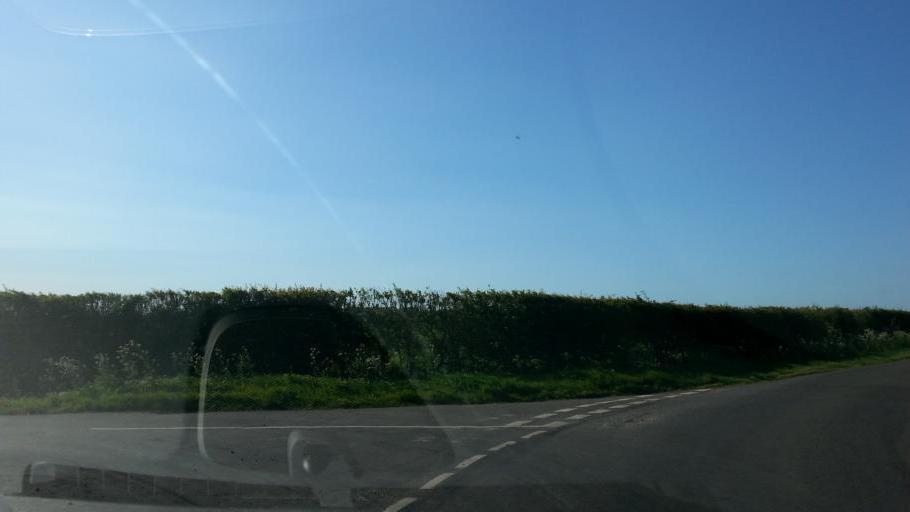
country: GB
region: England
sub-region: Lincolnshire
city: Long Bennington
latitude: 52.9999
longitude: -0.7099
